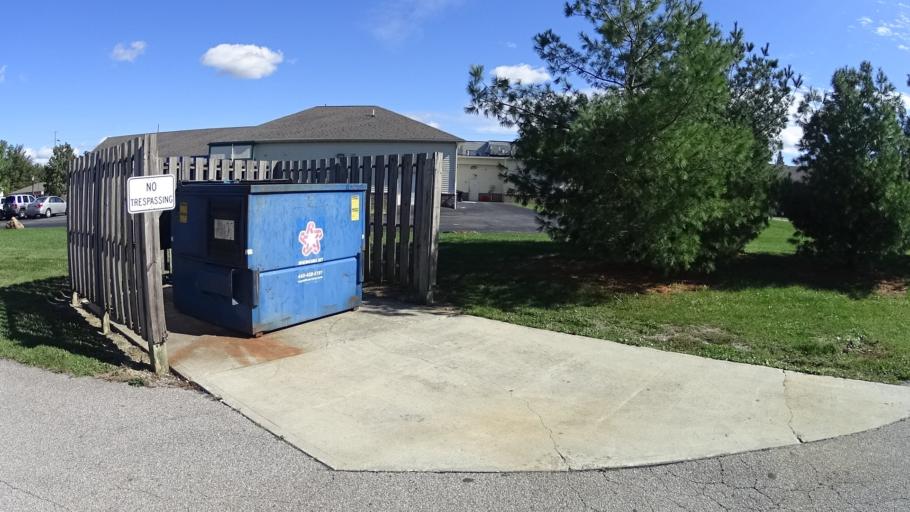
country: US
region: Ohio
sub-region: Lorain County
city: Grafton
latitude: 41.2792
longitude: -82.0644
